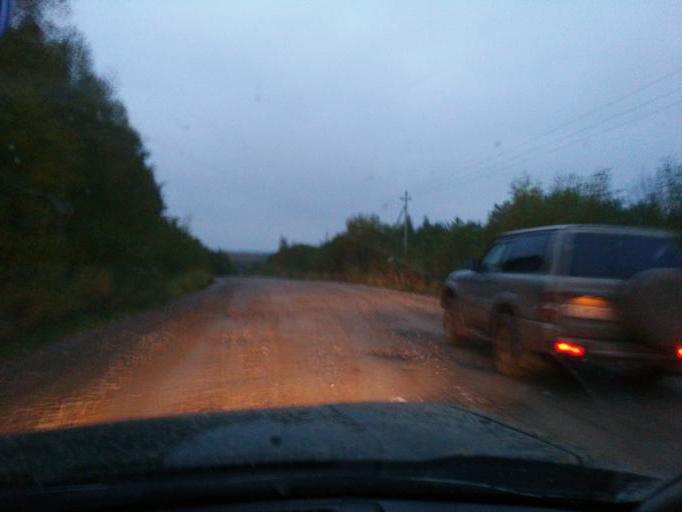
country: RU
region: Perm
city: Gornozavodsk
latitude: 57.9001
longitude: 58.4060
